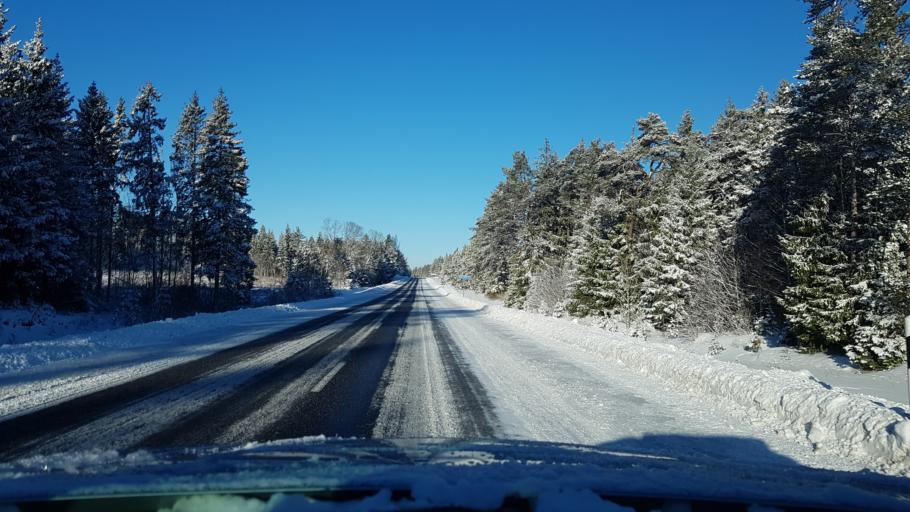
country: EE
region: Hiiumaa
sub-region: Kaerdla linn
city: Kardla
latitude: 58.9684
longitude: 22.8302
